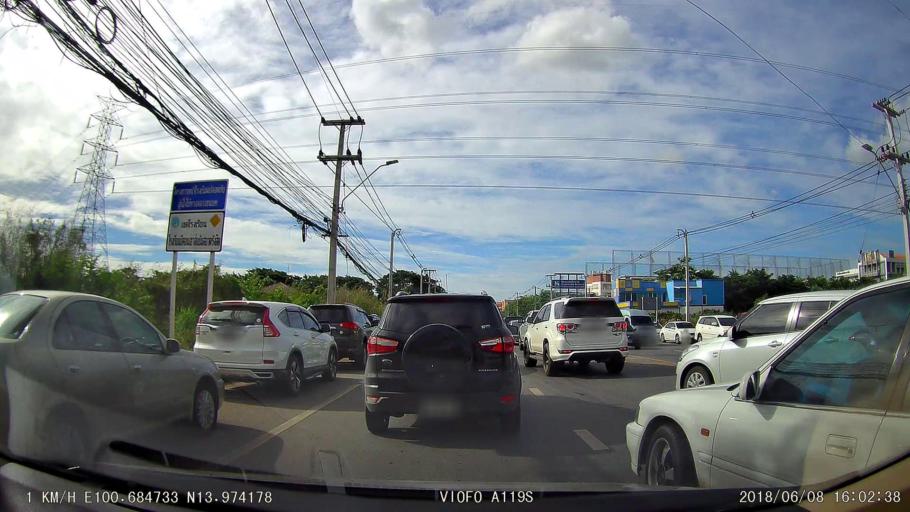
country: TH
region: Pathum Thani
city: Thanyaburi
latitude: 13.9789
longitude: 100.6850
